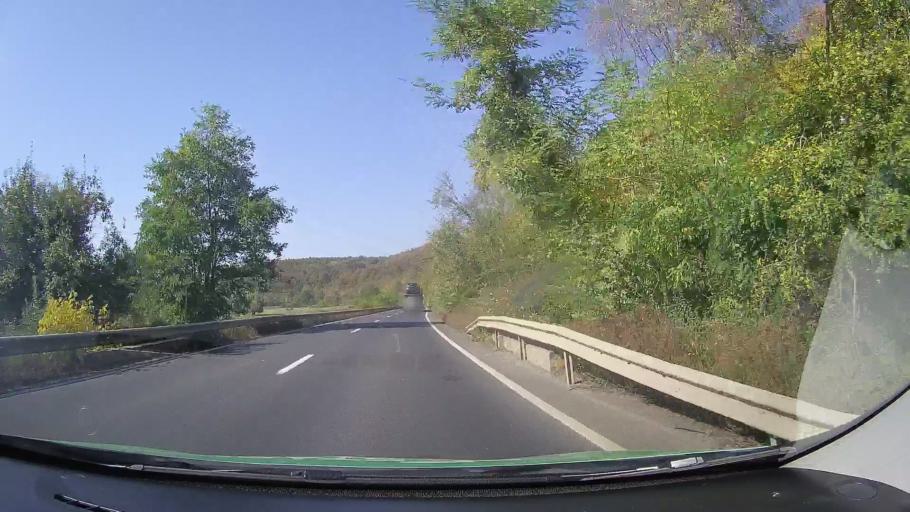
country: RO
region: Arad
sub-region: Comuna Bata
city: Bata
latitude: 46.0357
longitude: 22.0828
